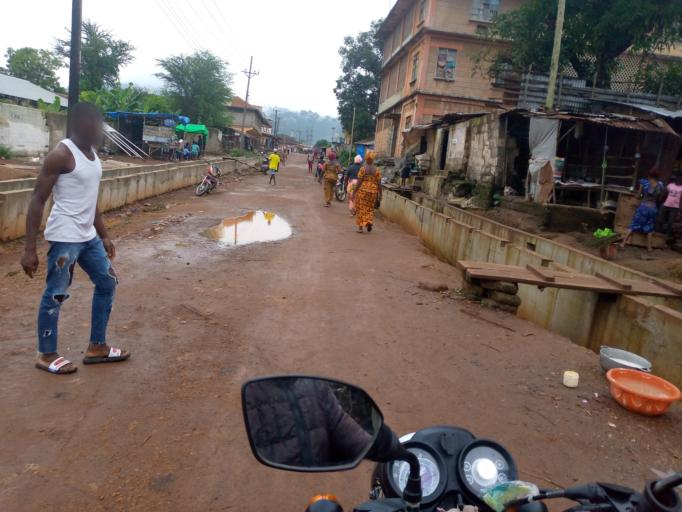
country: SL
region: Eastern Province
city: Kenema
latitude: 7.8794
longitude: -11.1865
